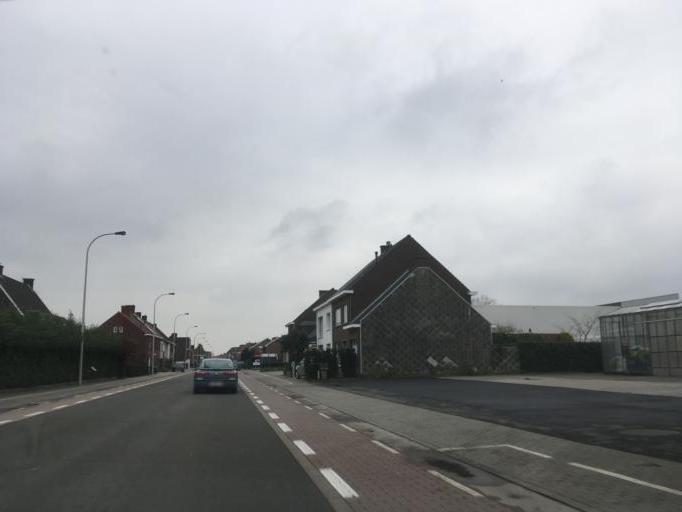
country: BE
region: Flanders
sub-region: Provincie West-Vlaanderen
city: Roeselare
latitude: 50.9473
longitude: 3.1034
